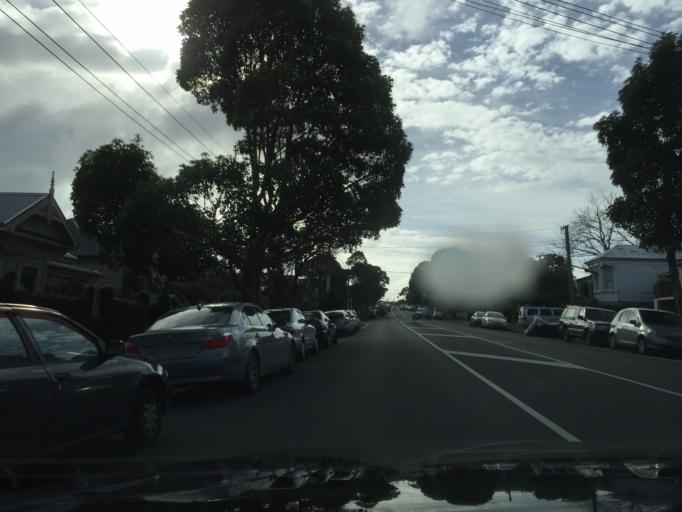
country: NZ
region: Auckland
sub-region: Auckland
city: Auckland
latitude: -36.8606
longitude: 174.7447
